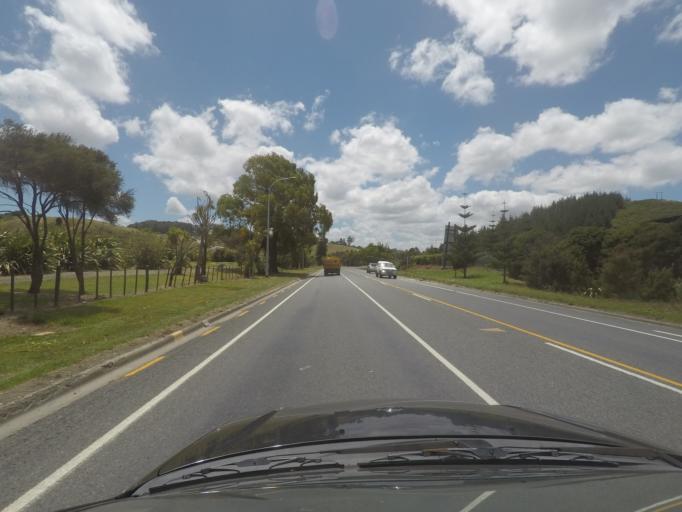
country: NZ
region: Northland
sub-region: Whangarei
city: Whangarei
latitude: -35.7503
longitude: 174.3205
